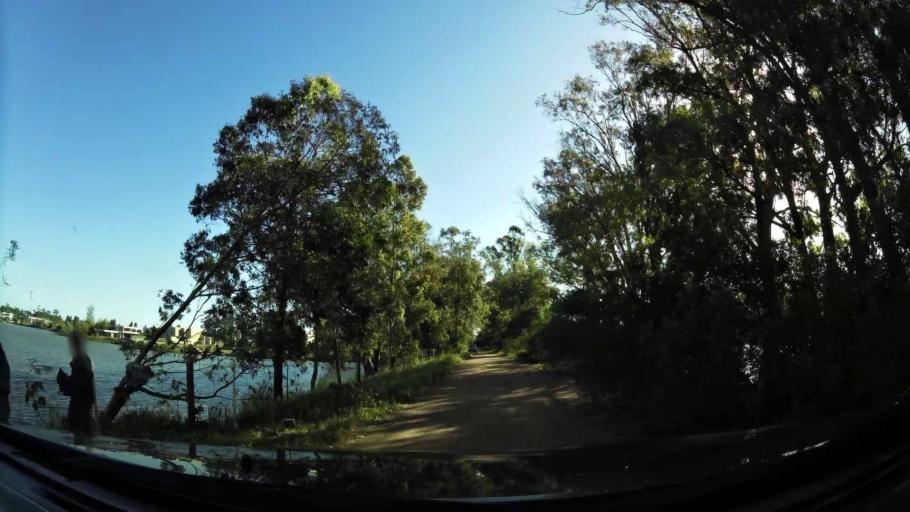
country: UY
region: Canelones
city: Paso de Carrasco
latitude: -34.8633
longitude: -56.0432
